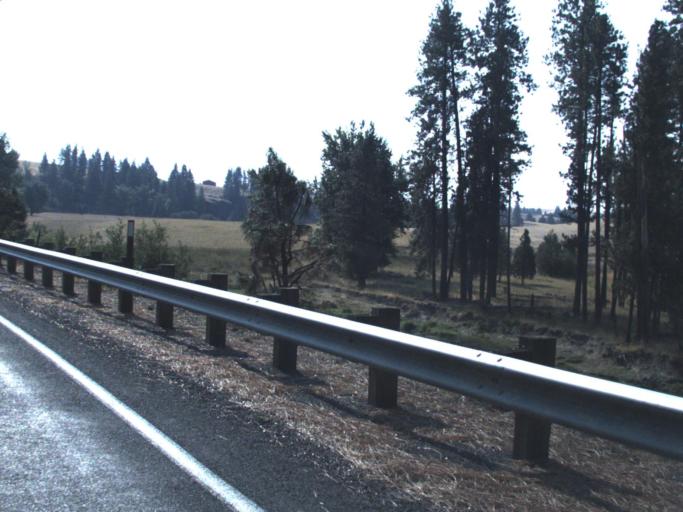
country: US
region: Washington
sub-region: Whitman County
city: Pullman
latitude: 46.9318
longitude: -117.0943
